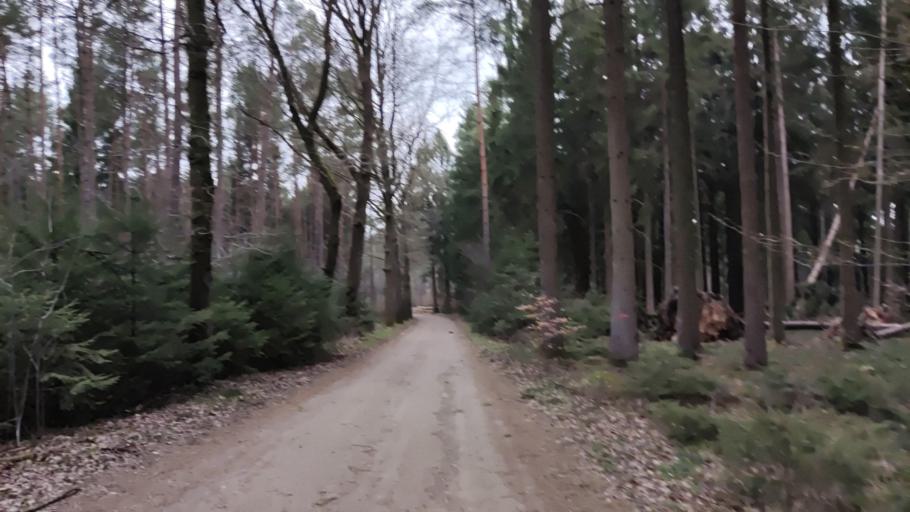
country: DE
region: Lower Saxony
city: Jesteburg
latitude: 53.2908
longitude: 9.9441
